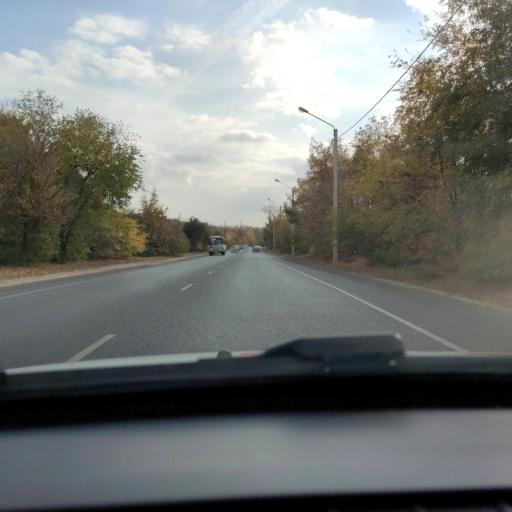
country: RU
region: Voronezj
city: Voronezh
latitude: 51.6111
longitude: 39.1793
